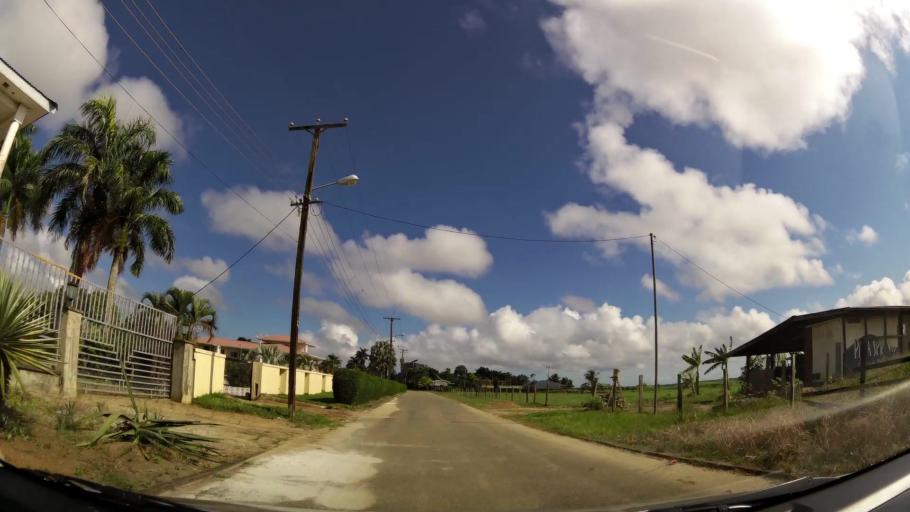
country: SR
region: Commewijne
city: Nieuw Amsterdam
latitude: 5.8708
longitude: -55.0998
